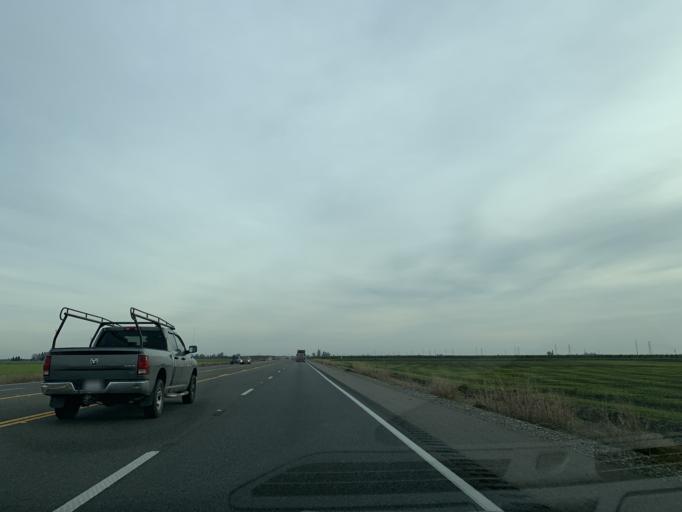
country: US
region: California
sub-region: Yuba County
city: Plumas Lake
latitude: 38.8801
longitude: -121.5661
